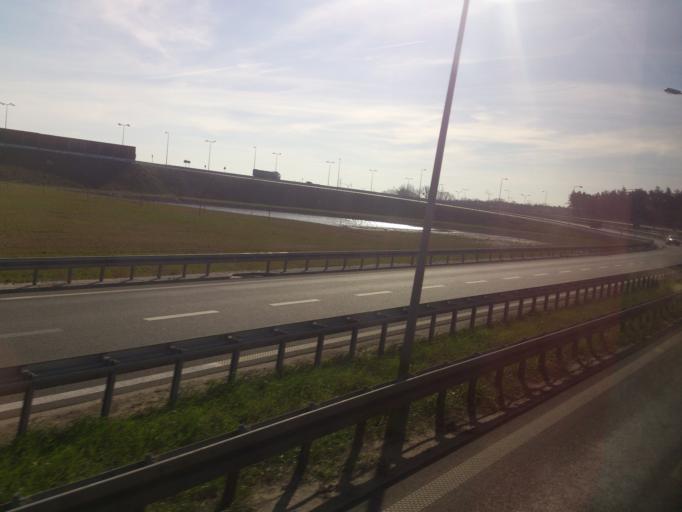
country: PL
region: Kujawsko-Pomorskie
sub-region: Powiat aleksandrowski
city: Ciechocinek
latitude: 52.8672
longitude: 18.7555
